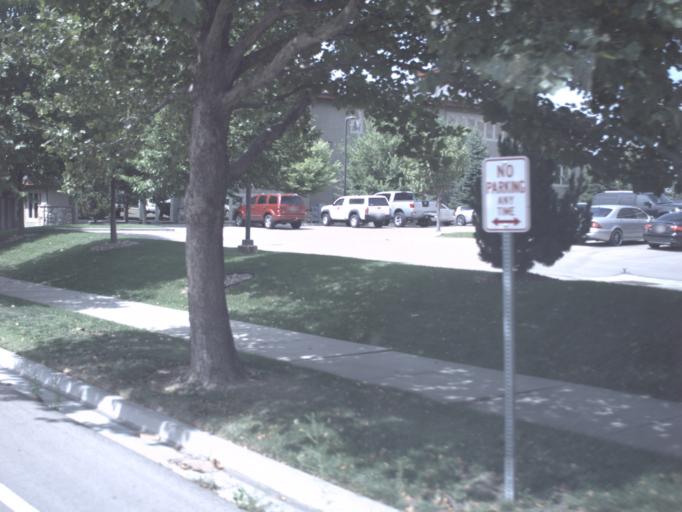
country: US
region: Utah
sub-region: Utah County
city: Lehi
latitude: 40.4312
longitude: -111.8971
